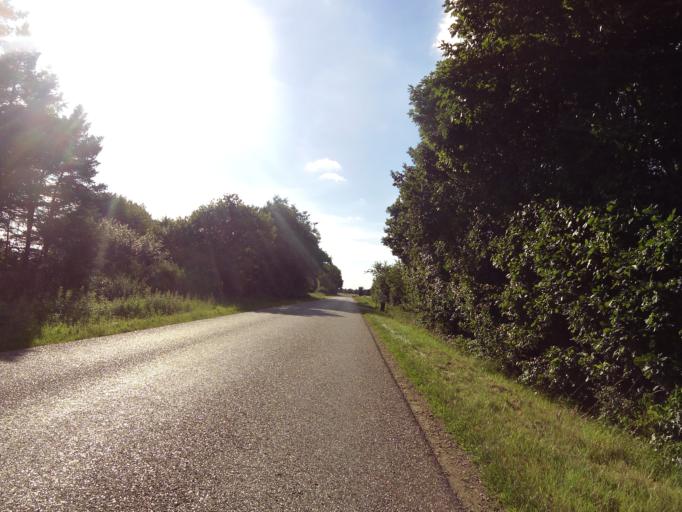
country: DK
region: South Denmark
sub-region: Haderslev Kommune
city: Vojens
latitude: 55.2044
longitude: 9.2783
